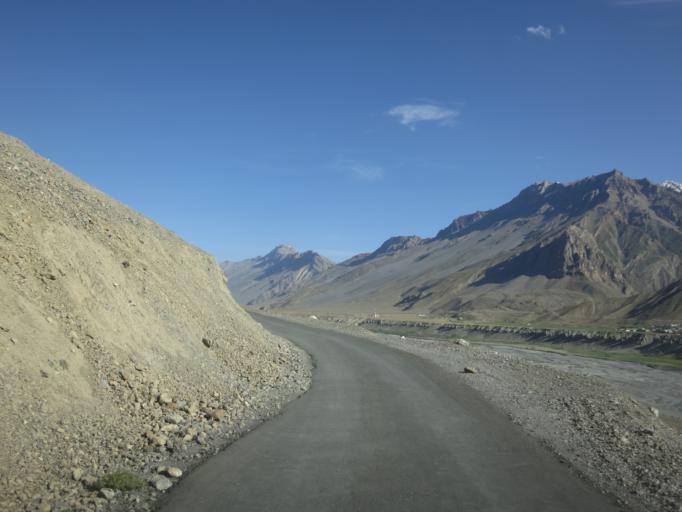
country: IN
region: Himachal Pradesh
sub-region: Shimla
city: Sarahan
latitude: 32.2747
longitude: 78.0279
